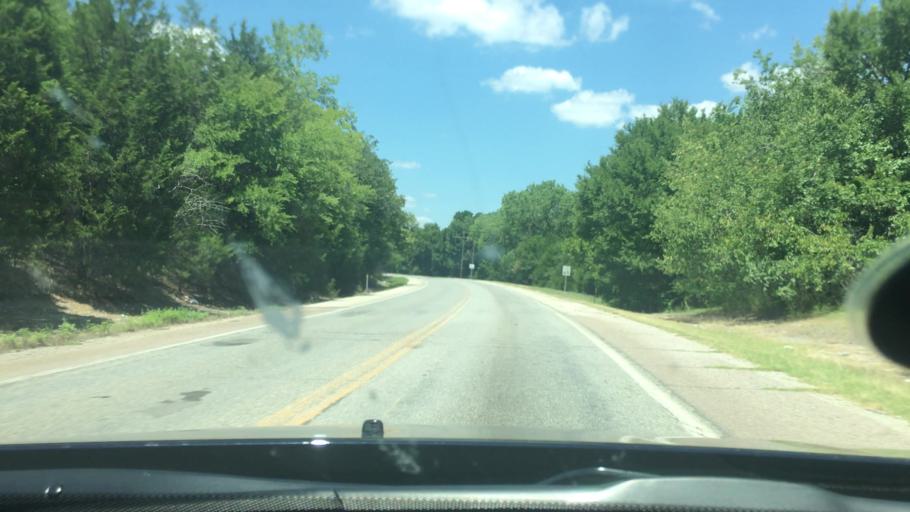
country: US
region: Oklahoma
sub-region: Marshall County
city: Oakland
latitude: 34.1721
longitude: -96.8369
